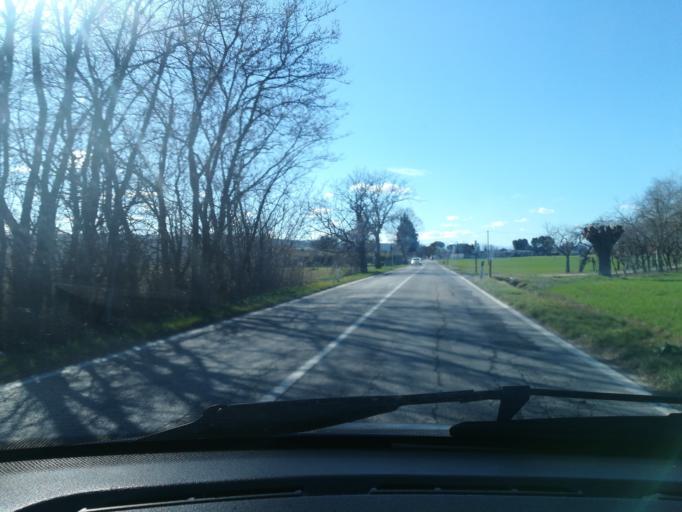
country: IT
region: The Marches
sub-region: Provincia di Macerata
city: Villa Potenza
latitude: 43.3336
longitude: 13.4267
